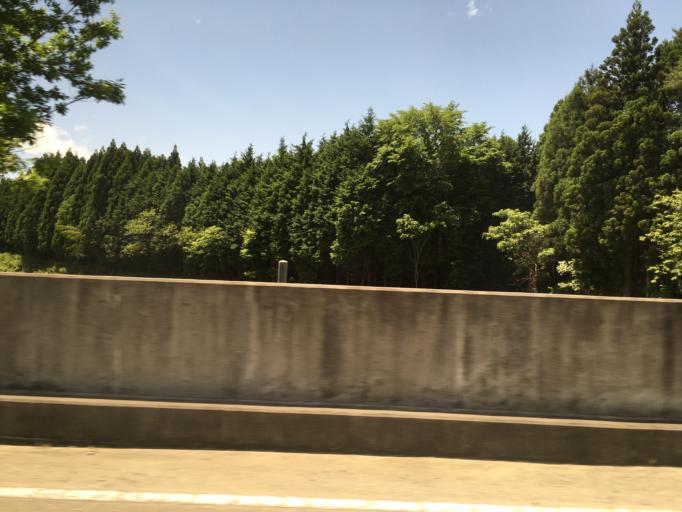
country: JP
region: Fukushima
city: Namie
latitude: 37.5081
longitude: 140.9759
